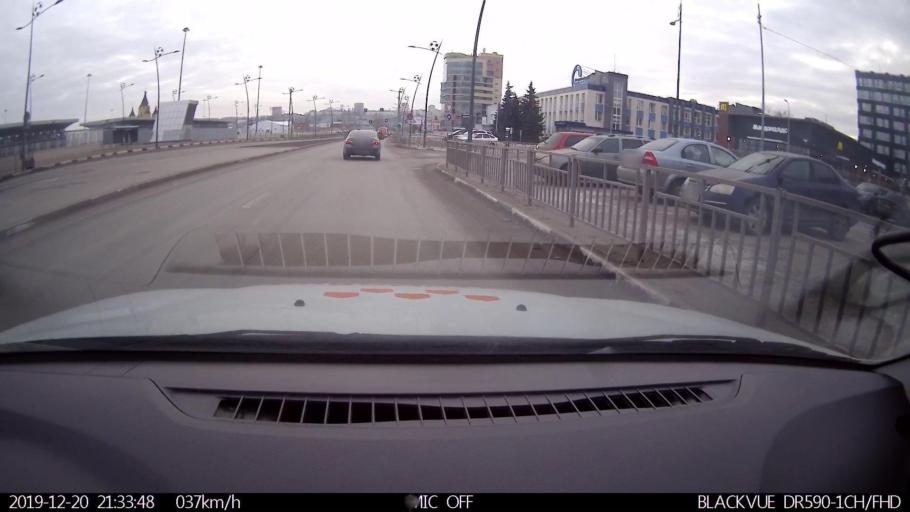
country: RU
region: Nizjnij Novgorod
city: Nizhniy Novgorod
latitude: 56.3350
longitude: 43.9624
